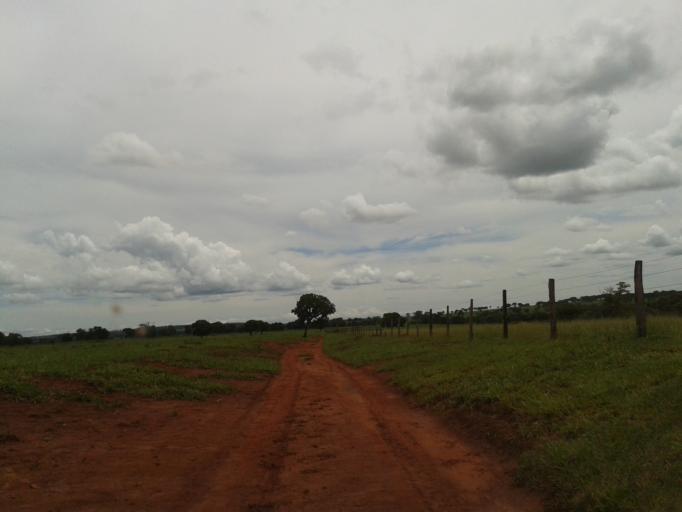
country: BR
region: Minas Gerais
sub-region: Santa Vitoria
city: Santa Vitoria
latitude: -18.7872
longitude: -49.8527
